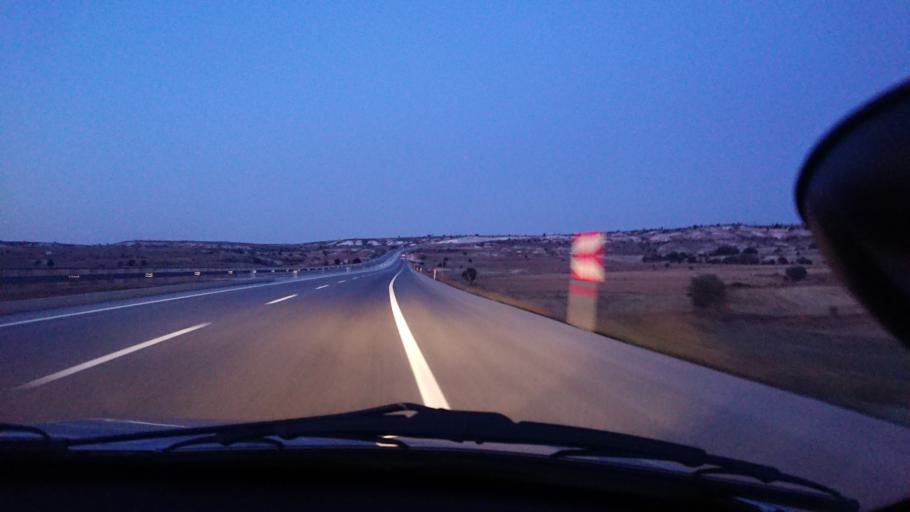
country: TR
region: Kuetahya
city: Cavdarhisar
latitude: 39.1332
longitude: 29.5532
